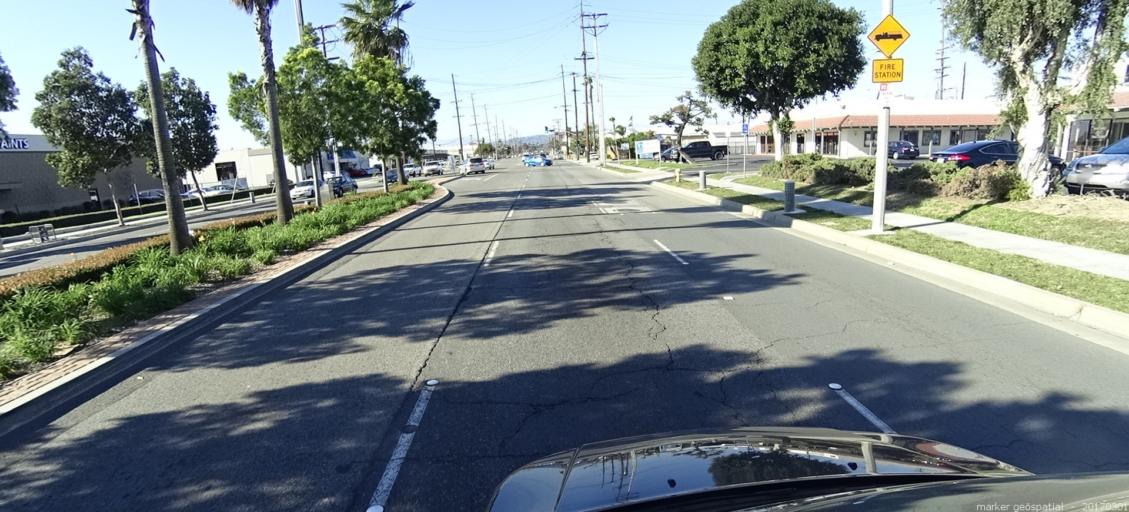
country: US
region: California
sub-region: Orange County
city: Placentia
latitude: 33.8521
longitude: -117.8576
